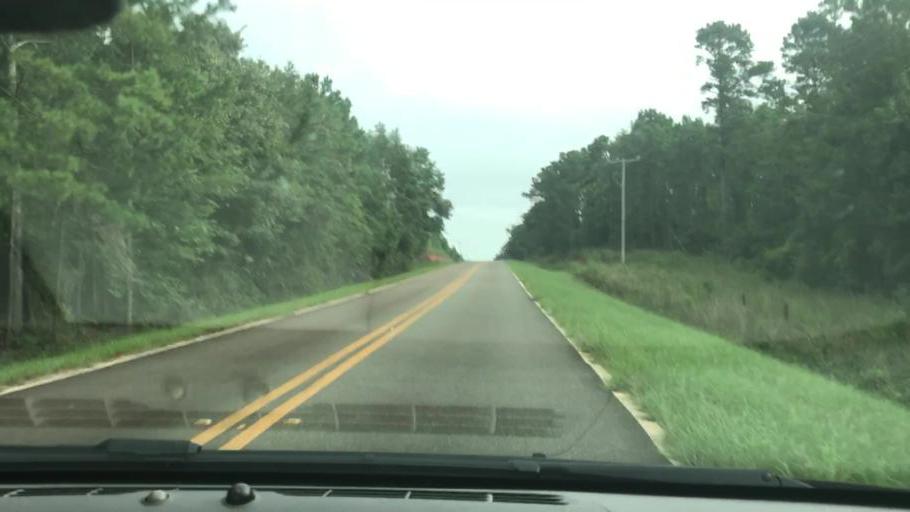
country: US
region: Georgia
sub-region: Stewart County
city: Lumpkin
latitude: 32.0289
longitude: -84.9120
